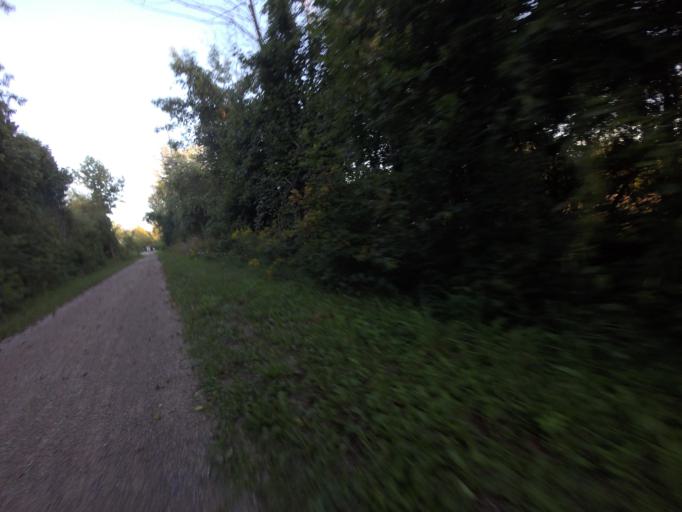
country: CA
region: Ontario
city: Goderich
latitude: 43.7544
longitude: -81.6724
